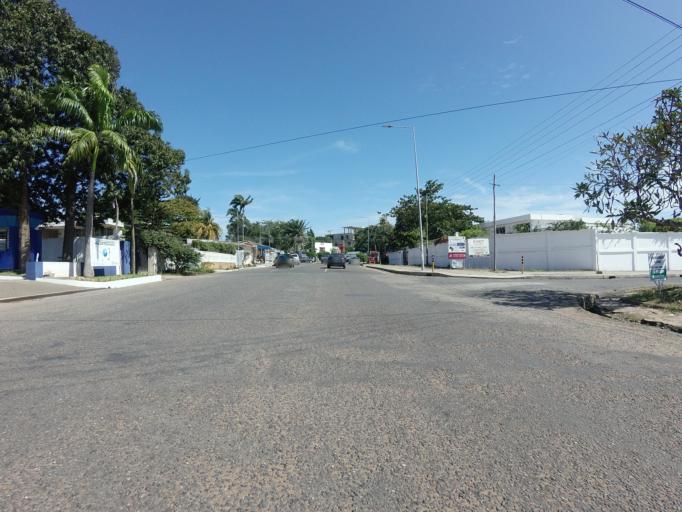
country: GH
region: Greater Accra
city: Accra
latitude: 5.5712
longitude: -0.1691
